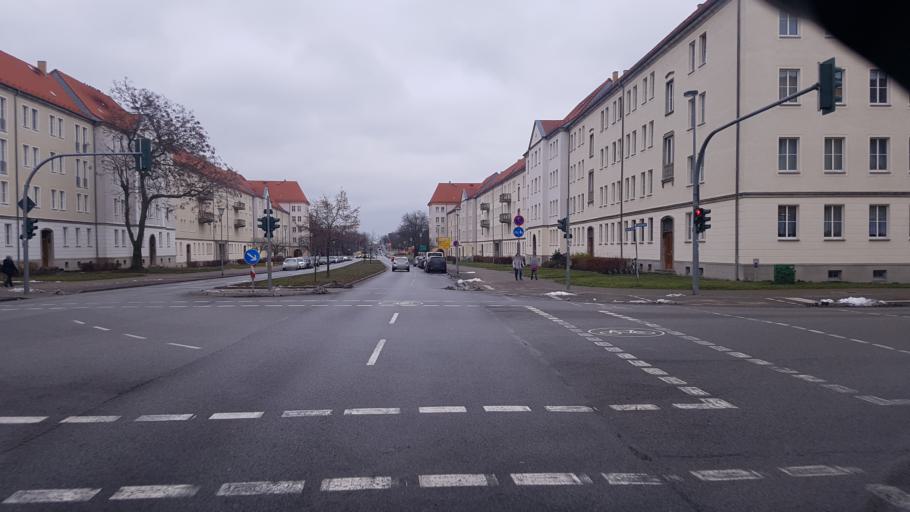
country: DE
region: Brandenburg
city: Eisenhuettenstadt
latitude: 52.1457
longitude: 14.6308
